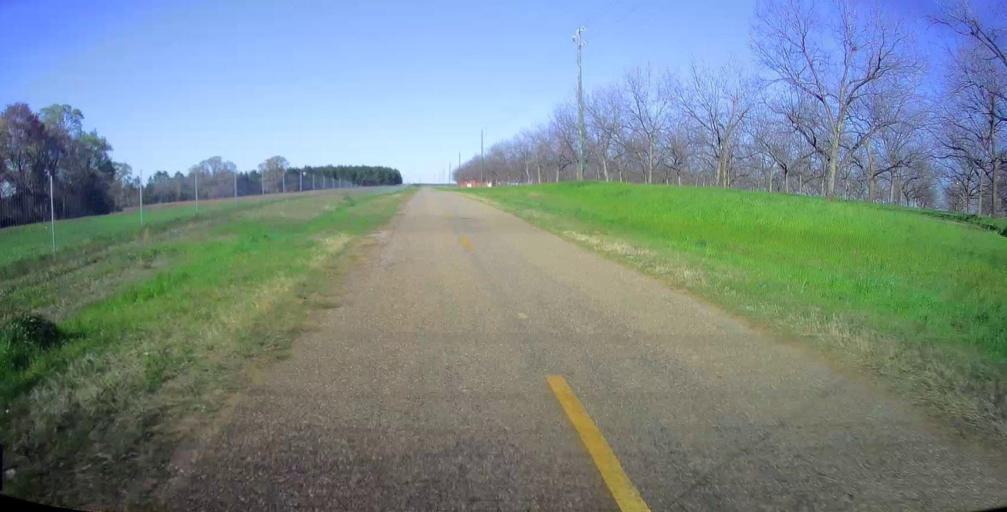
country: US
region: Georgia
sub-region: Macon County
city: Marshallville
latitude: 32.5018
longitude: -83.9508
